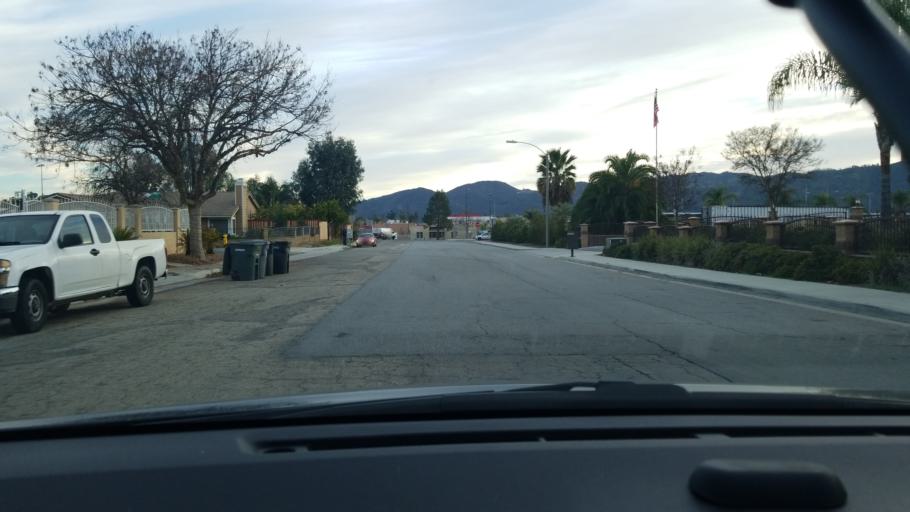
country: US
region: California
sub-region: Riverside County
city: Sedco Hills
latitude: 33.6281
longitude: -117.2797
